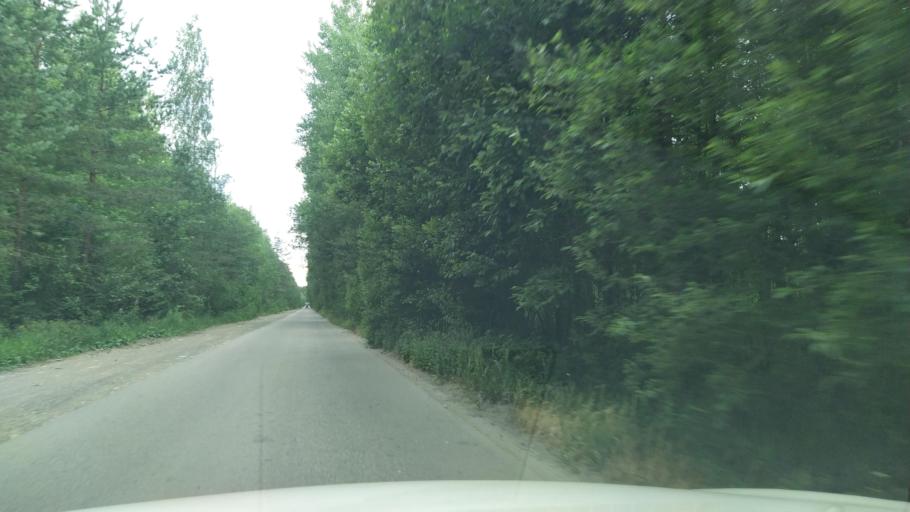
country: RU
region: St.-Petersburg
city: Bol'shaya Izhora
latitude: 59.9165
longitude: 29.5695
